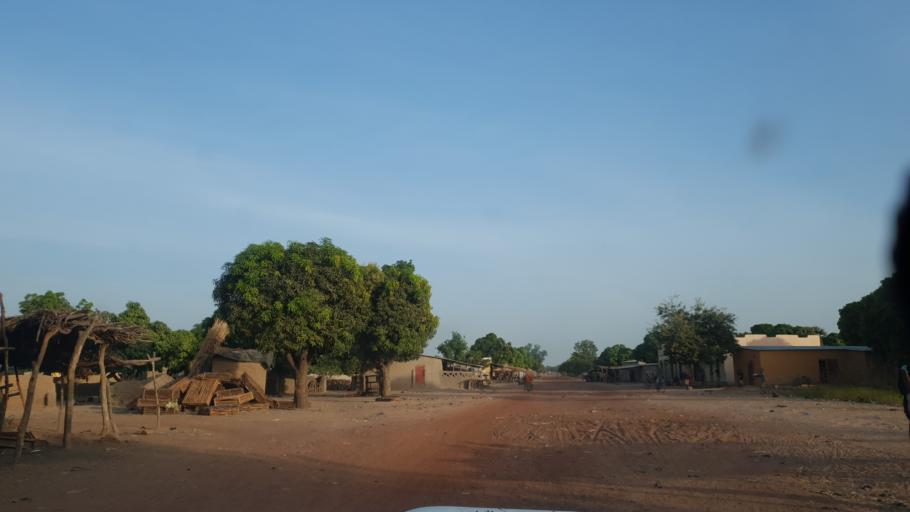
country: ML
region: Koulikoro
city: Dioila
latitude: 12.4759
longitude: -6.4063
